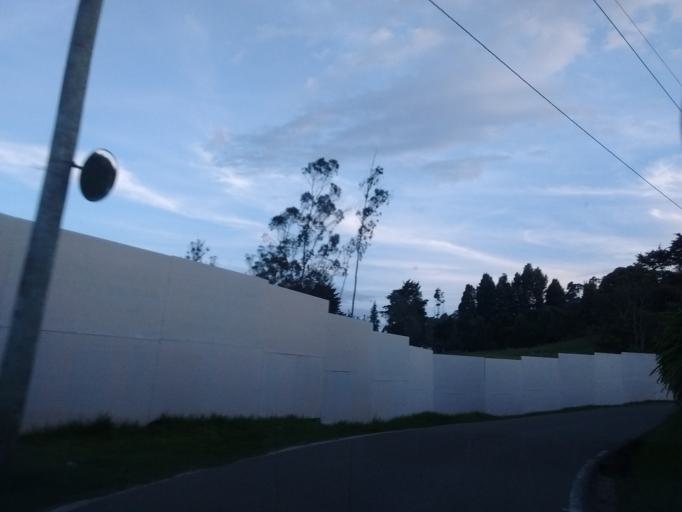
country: CO
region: Antioquia
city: Envigado
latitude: 6.1737
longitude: -75.5030
